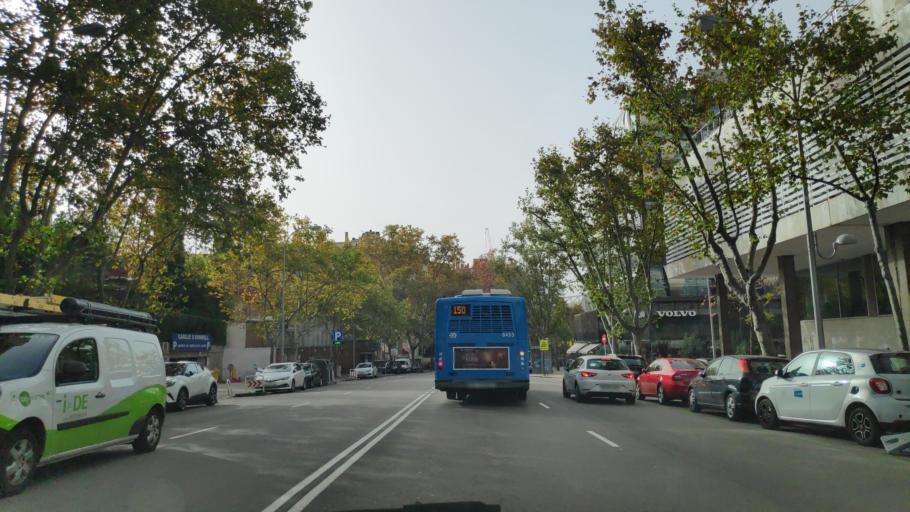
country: ES
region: Madrid
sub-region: Provincia de Madrid
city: Chamartin
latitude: 40.4582
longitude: -3.6856
